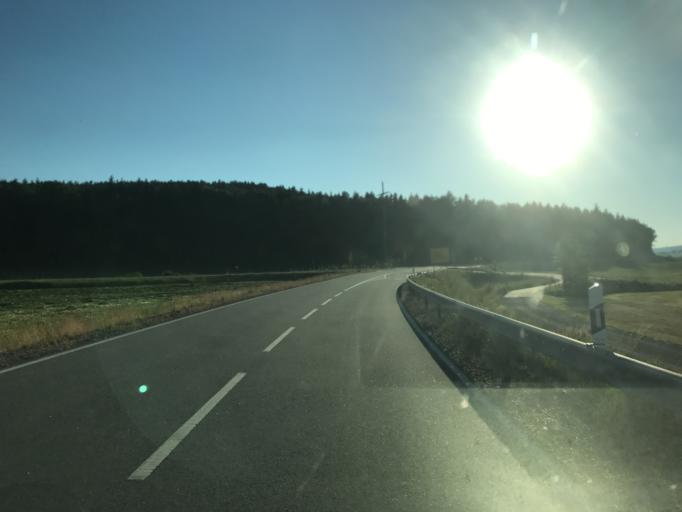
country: DE
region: Bavaria
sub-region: Upper Palatinate
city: Waldmunchen
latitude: 49.3782
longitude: 12.6808
